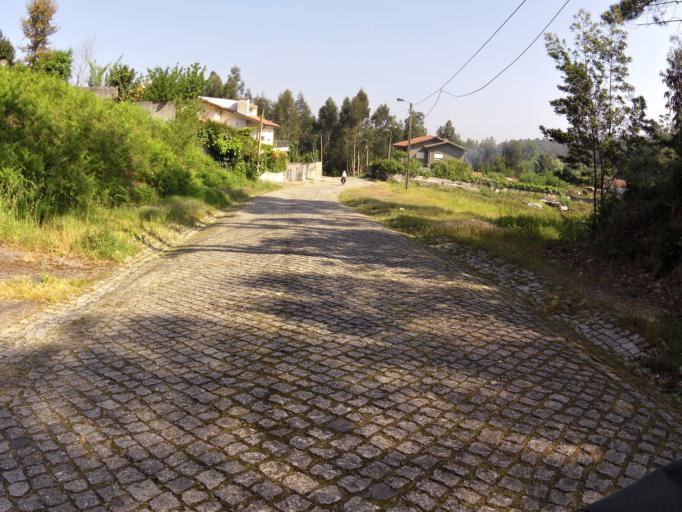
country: PT
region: Porto
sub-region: Vila Nova de Gaia
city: Olival
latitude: 41.0446
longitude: -8.5359
